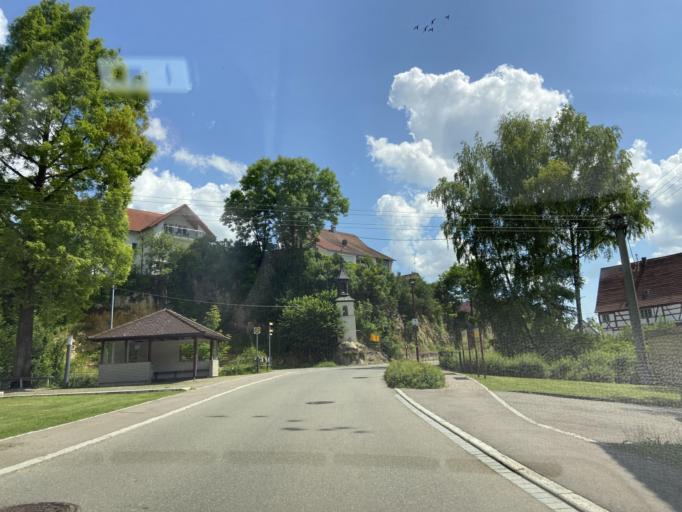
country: DE
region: Baden-Wuerttemberg
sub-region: Tuebingen Region
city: Veringenstadt
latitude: 48.1583
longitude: 9.2023
